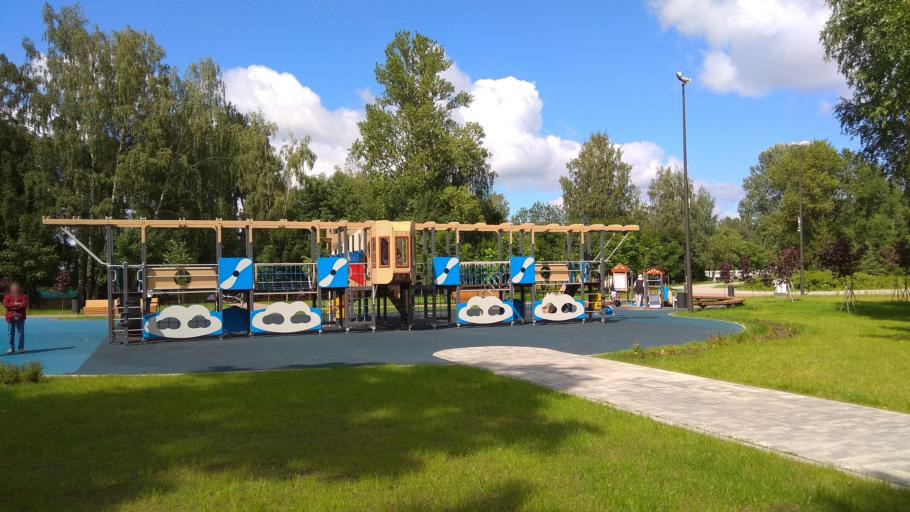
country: RU
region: St.-Petersburg
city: Krasnogvargeisky
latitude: 59.9631
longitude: 30.4701
